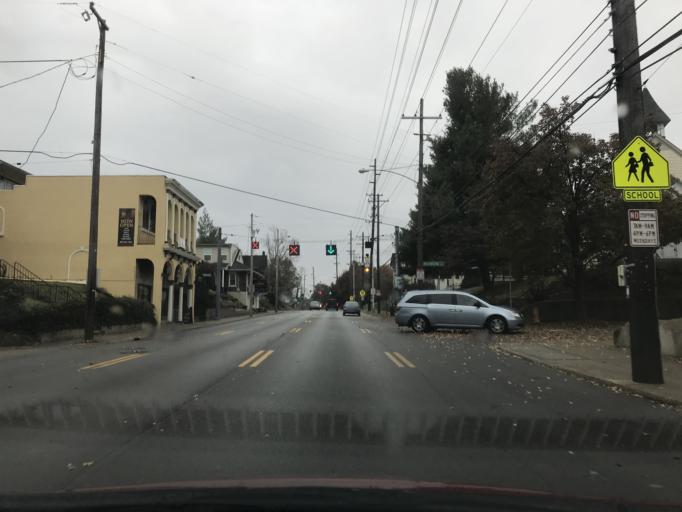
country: US
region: Kentucky
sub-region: Jefferson County
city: Audubon Park
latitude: 38.2272
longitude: -85.6992
